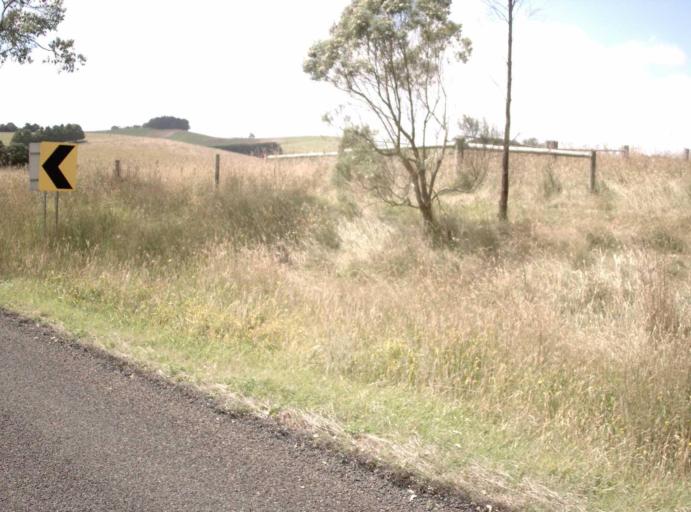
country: AU
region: Victoria
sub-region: Cardinia
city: Bunyip
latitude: -38.3322
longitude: 145.7159
